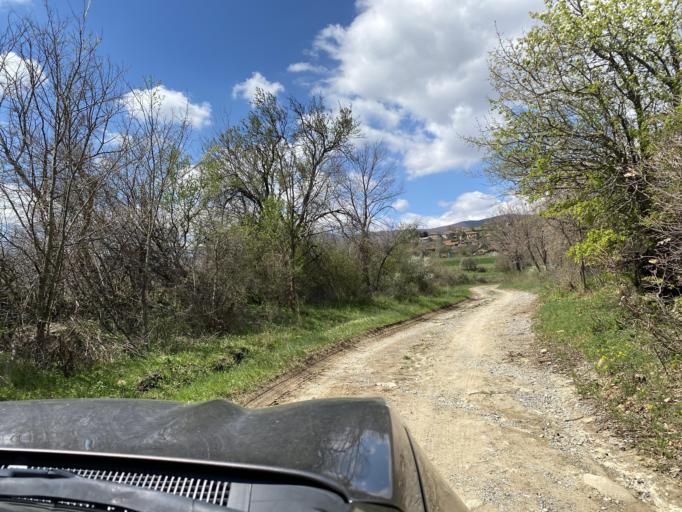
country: MK
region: Caska
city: Caska
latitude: 41.7352
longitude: 21.6465
